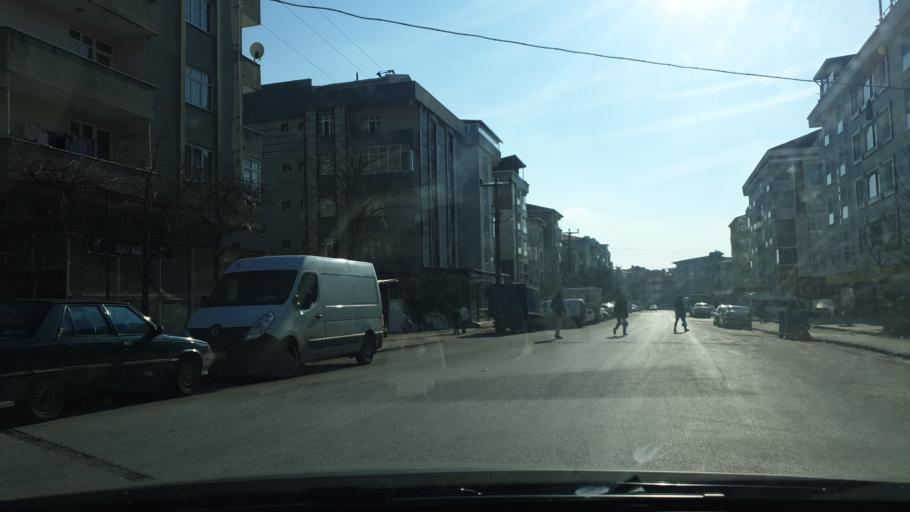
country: TR
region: Tekirdag
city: Cerkezkoey
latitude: 41.2862
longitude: 27.9853
